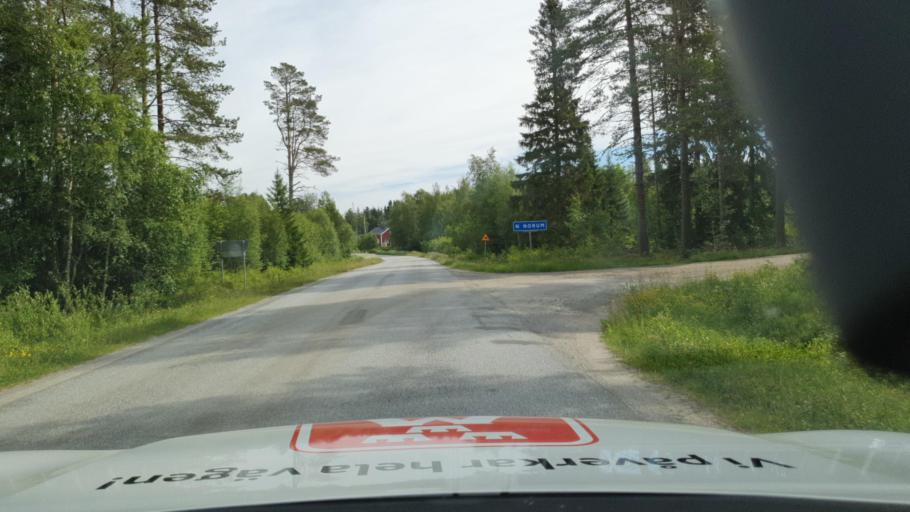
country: SE
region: Vaesterbotten
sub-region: Umea Kommun
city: Saevar
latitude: 63.8973
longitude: 20.7620
